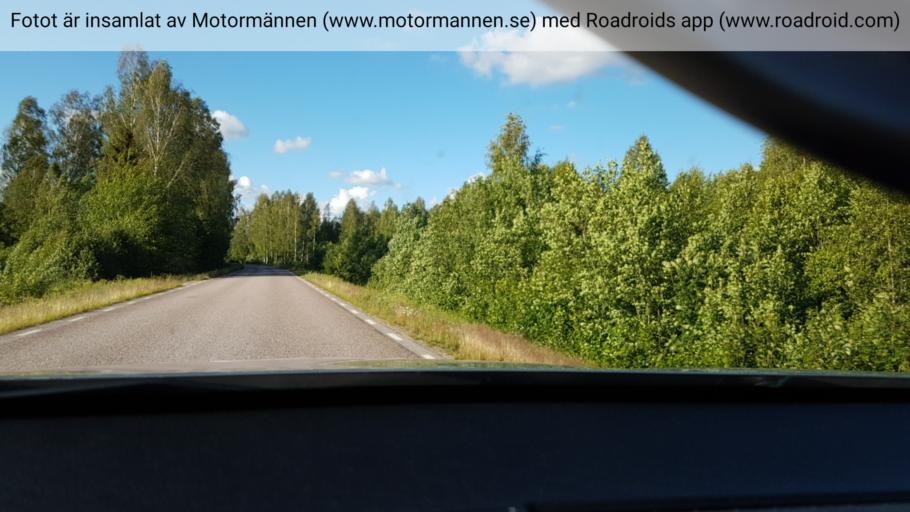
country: SE
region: Vaermland
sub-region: Hagfors Kommun
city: Hagfors
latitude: 60.0675
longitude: 13.5666
